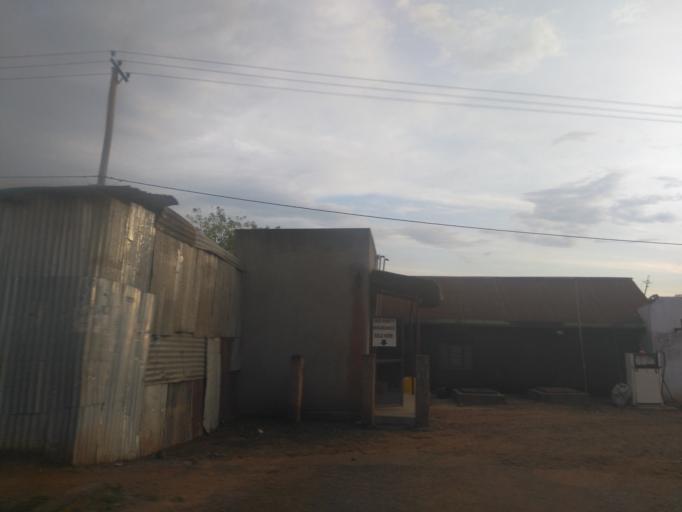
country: UG
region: Central Region
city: Kampala Central Division
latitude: 0.3824
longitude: 32.5665
